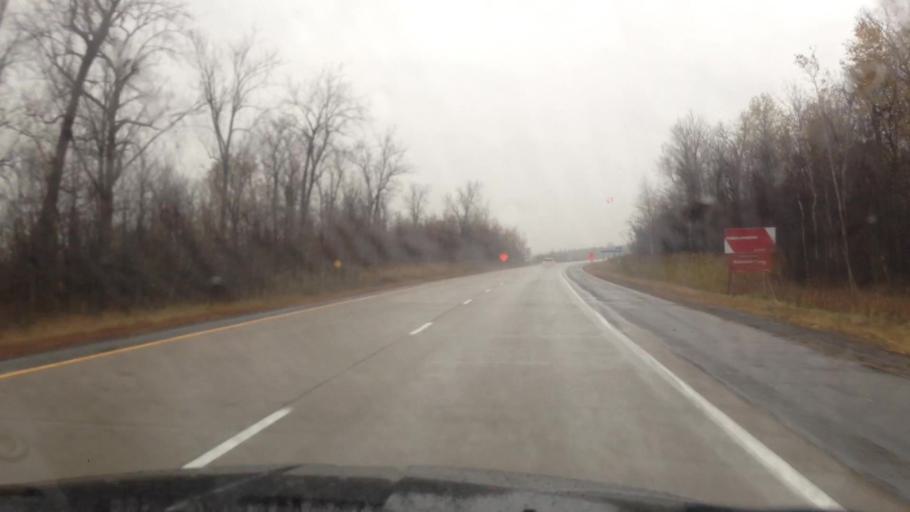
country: CA
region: Ontario
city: Hawkesbury
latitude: 45.4221
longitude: -74.7637
